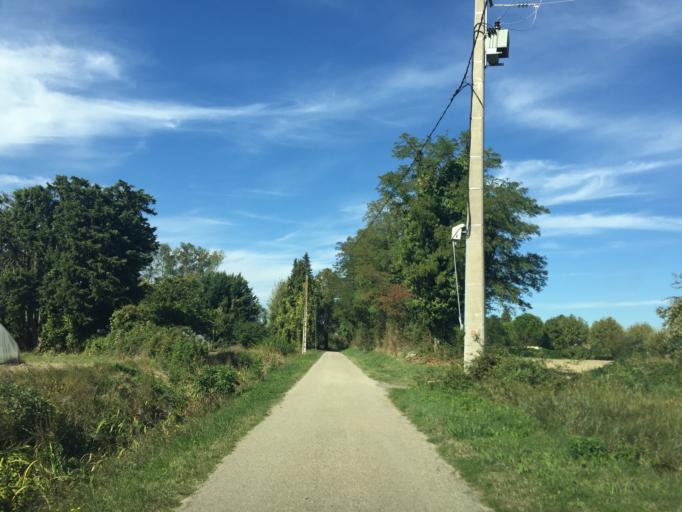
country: FR
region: Provence-Alpes-Cote d'Azur
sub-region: Departement du Vaucluse
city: Mornas
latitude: 44.1761
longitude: 4.7356
